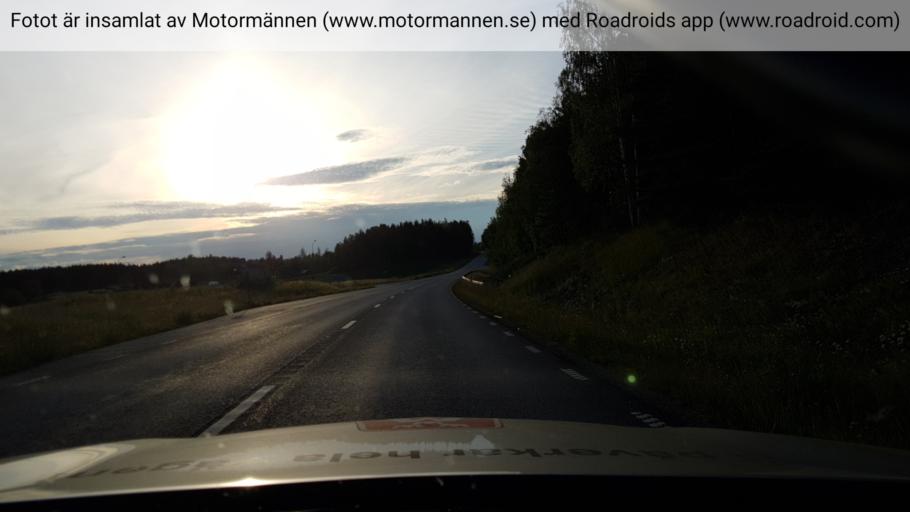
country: SE
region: OErebro
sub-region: Lindesbergs Kommun
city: Lindesberg
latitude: 59.5308
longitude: 15.2712
